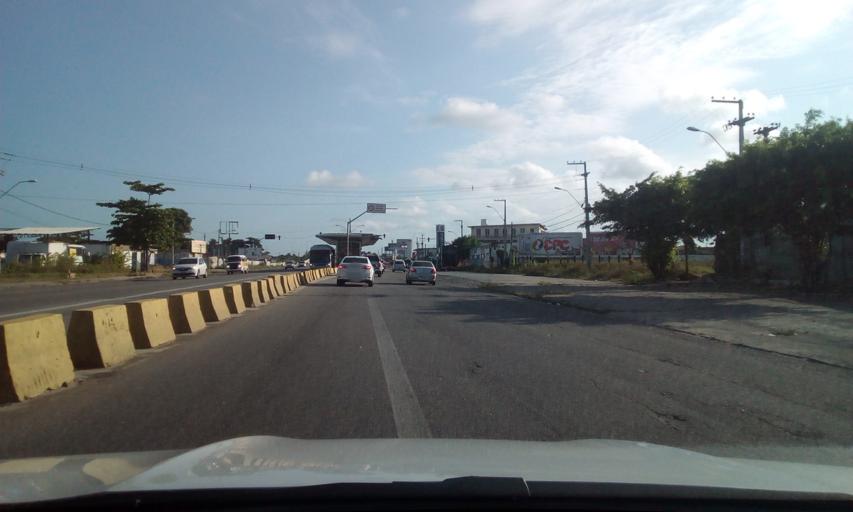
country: BR
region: Pernambuco
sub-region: Olinda
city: Olinda
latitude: -8.0139
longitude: -34.8596
